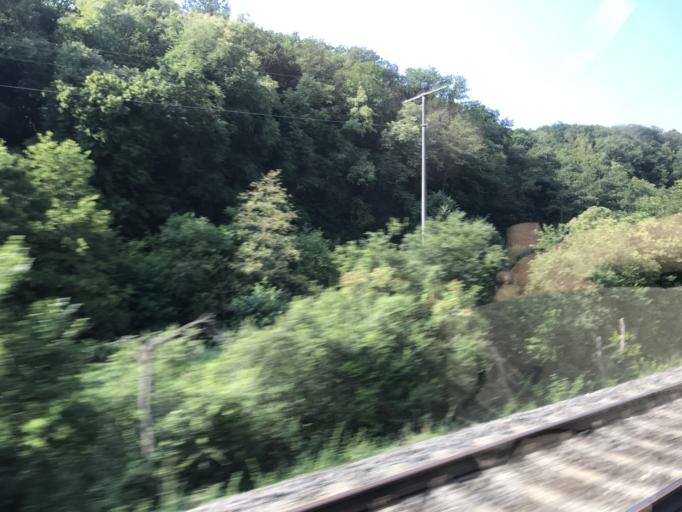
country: DE
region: Hesse
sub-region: Regierungsbezirk Giessen
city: Villmar
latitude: 50.3482
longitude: 8.2024
